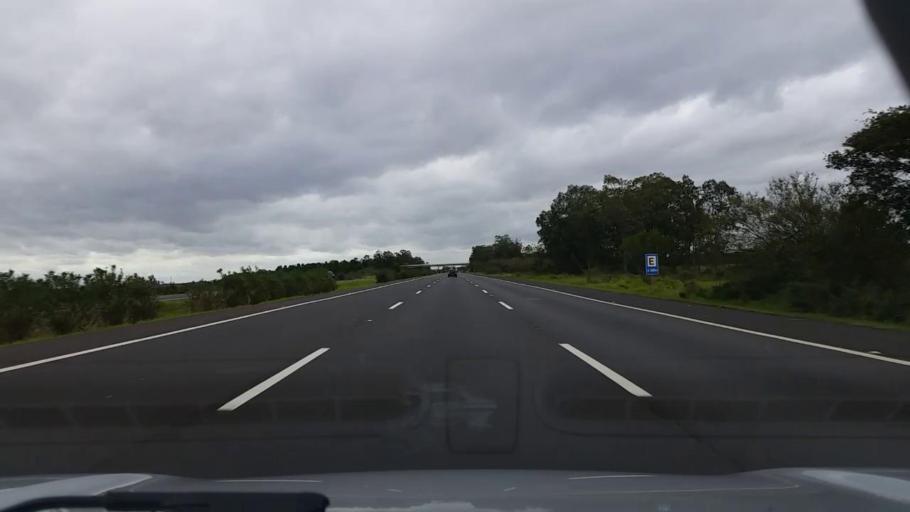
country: BR
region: Rio Grande do Sul
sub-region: Rolante
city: Rolante
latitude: -29.8845
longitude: -50.5719
